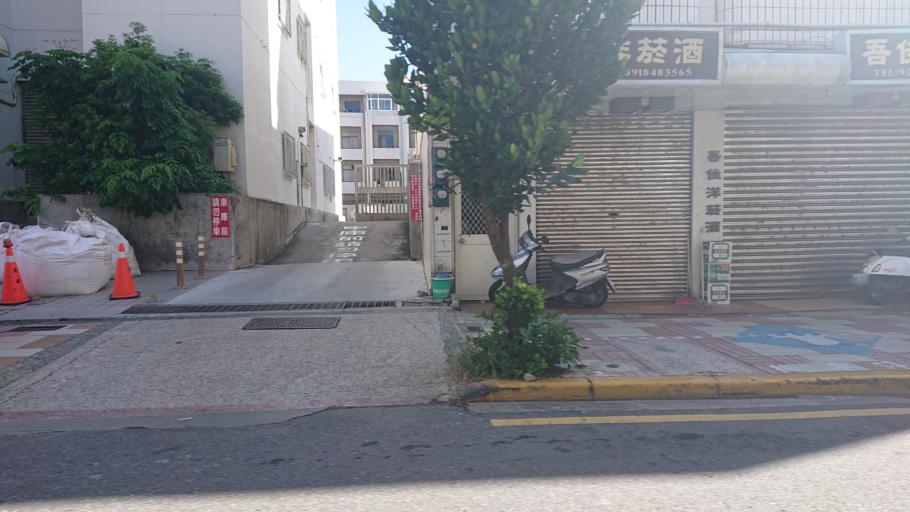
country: TW
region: Taiwan
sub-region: Penghu
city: Ma-kung
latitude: 23.5653
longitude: 119.5666
